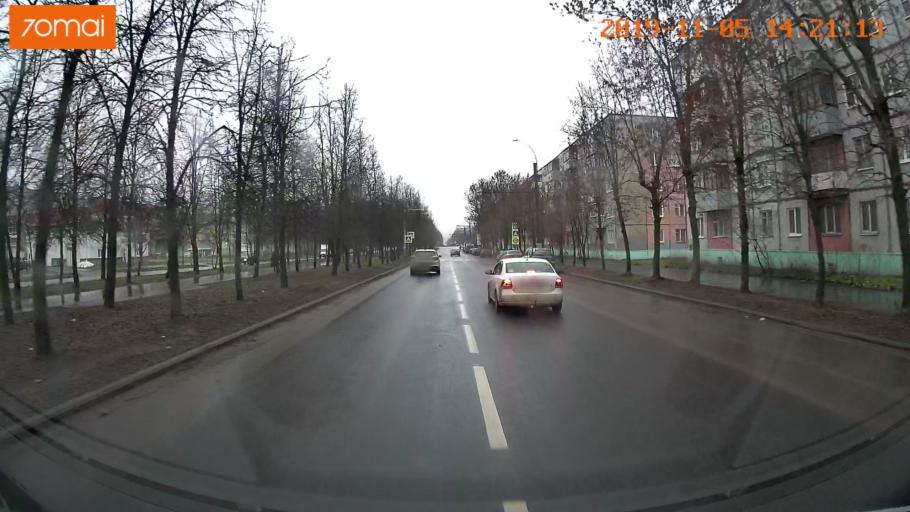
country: RU
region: Ivanovo
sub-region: Gorod Ivanovo
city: Ivanovo
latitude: 56.9580
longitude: 41.0126
